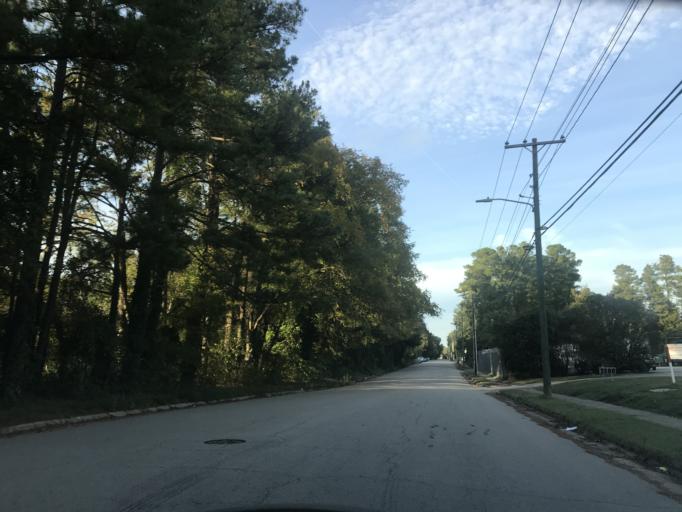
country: US
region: North Carolina
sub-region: Wake County
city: Raleigh
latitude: 35.8260
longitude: -78.6137
